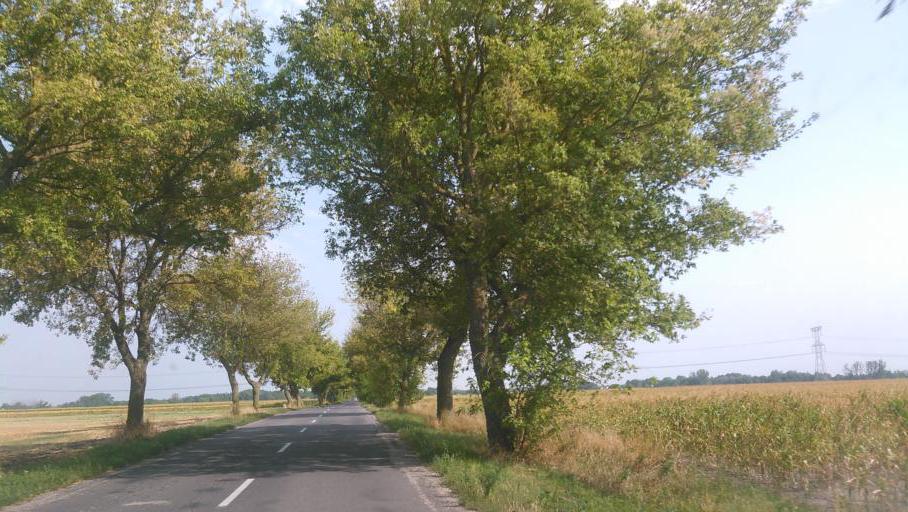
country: SK
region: Trnavsky
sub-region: Okres Dunajska Streda
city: Velky Meder
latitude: 47.9076
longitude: 17.7764
